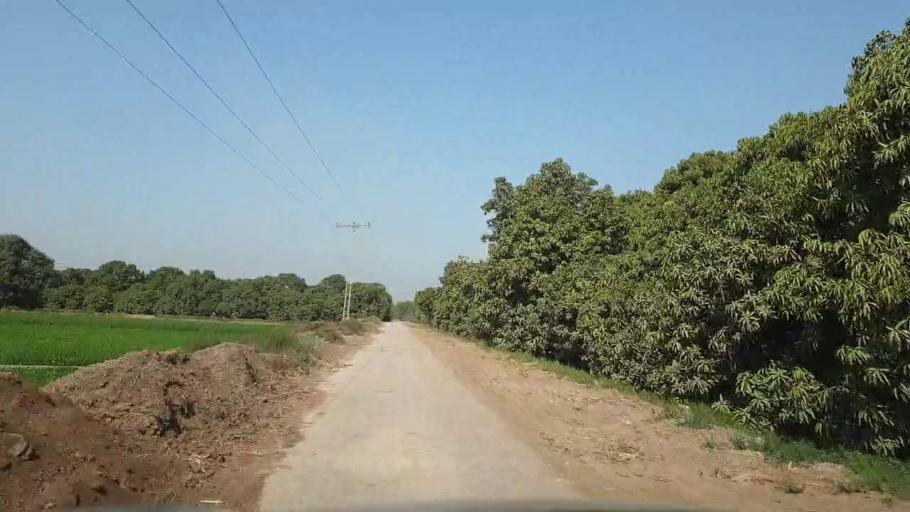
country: PK
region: Sindh
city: Tando Allahyar
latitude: 25.5573
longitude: 68.7092
